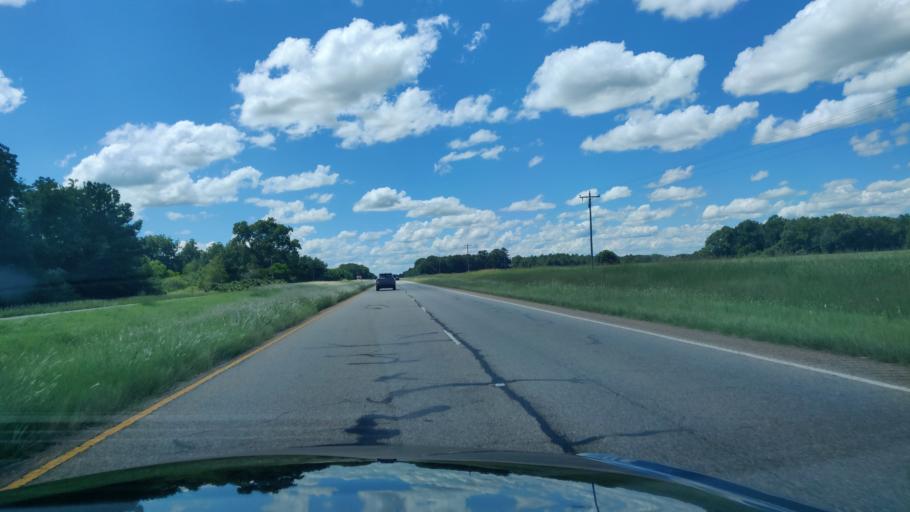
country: US
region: Georgia
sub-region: Webster County
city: Preston
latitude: 31.9541
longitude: -84.5845
